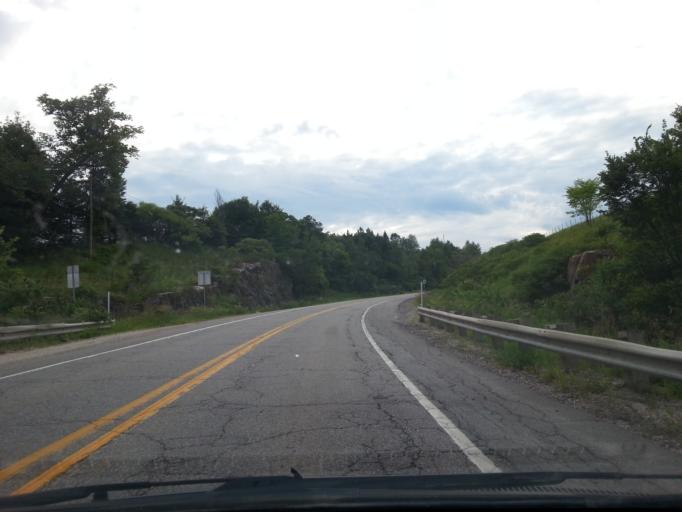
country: CA
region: Quebec
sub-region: Outaouais
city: Wakefield
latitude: 45.6522
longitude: -75.9247
